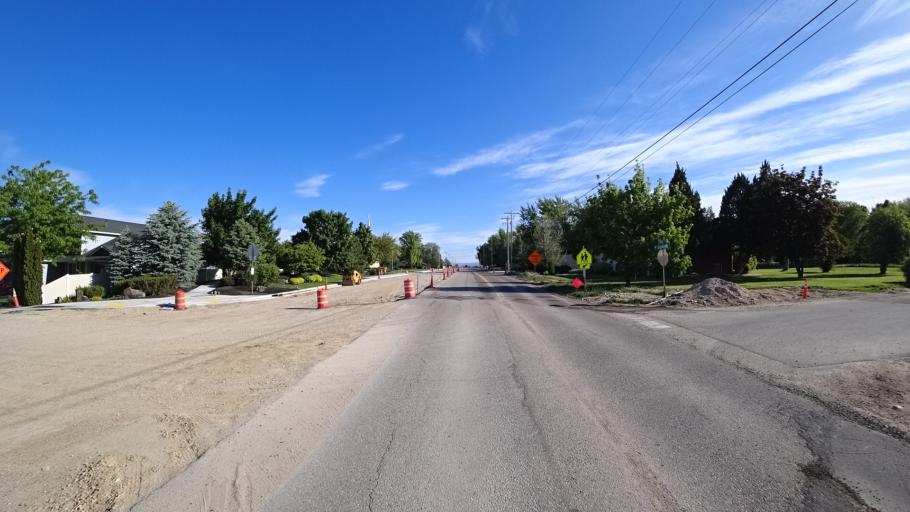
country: US
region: Idaho
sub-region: Ada County
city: Garden City
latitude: 43.5697
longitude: -116.2741
